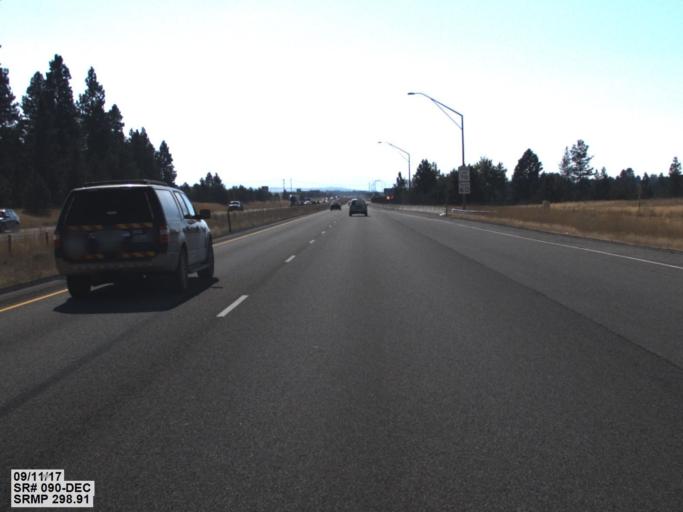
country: US
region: Washington
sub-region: Spokane County
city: Otis Orchards-East Farms
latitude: 47.6921
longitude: -117.0596
